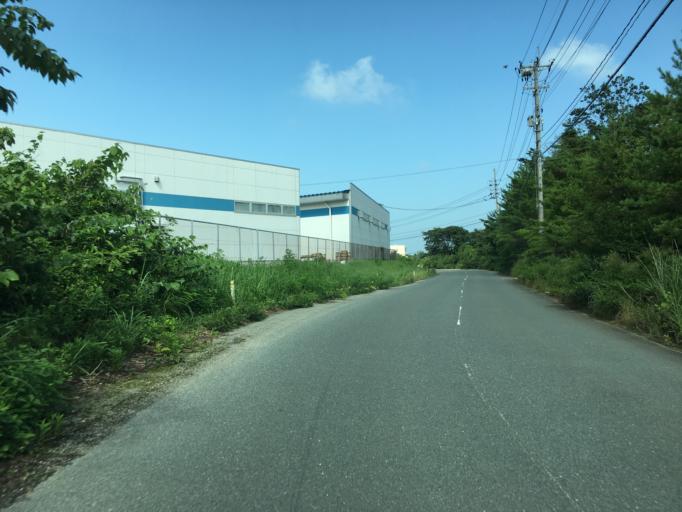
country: JP
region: Miyagi
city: Marumori
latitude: 37.8975
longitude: 140.8900
